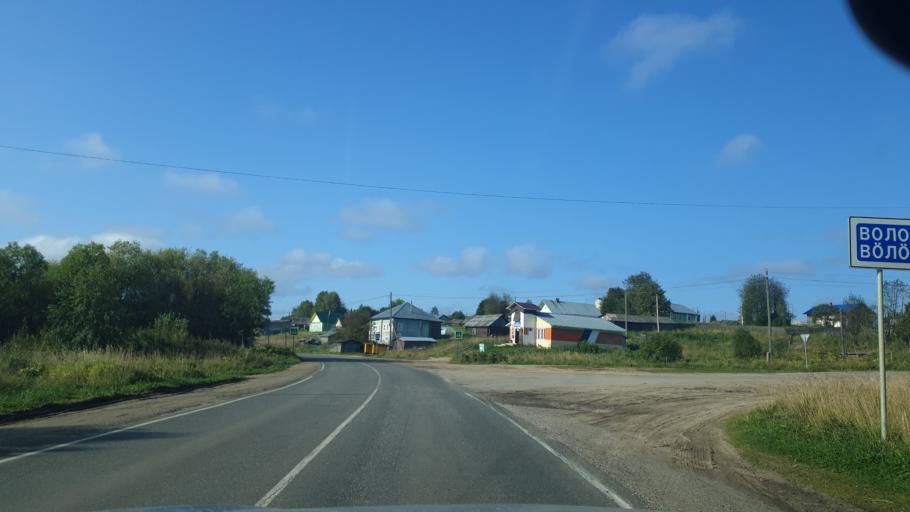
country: RU
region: Komi Republic
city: Vizinga
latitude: 60.9677
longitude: 50.2456
